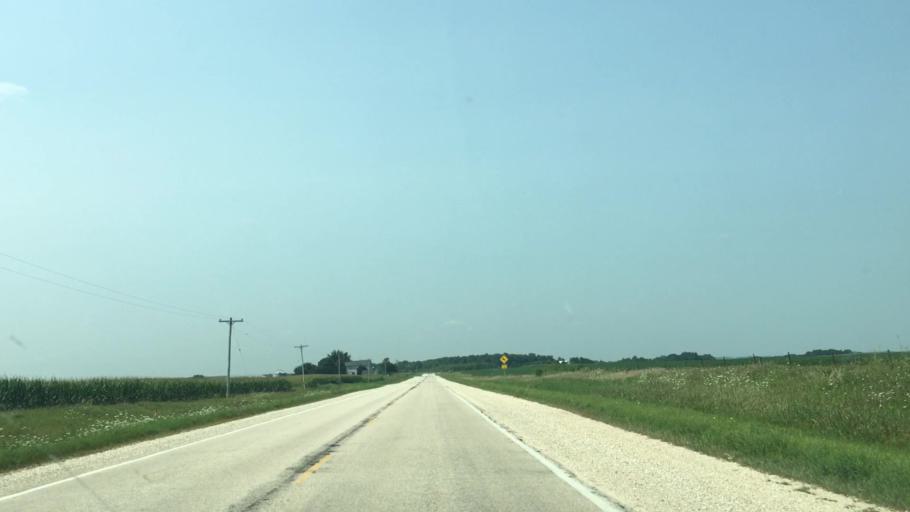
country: US
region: Iowa
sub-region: Fayette County
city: West Union
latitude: 43.0255
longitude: -91.8282
